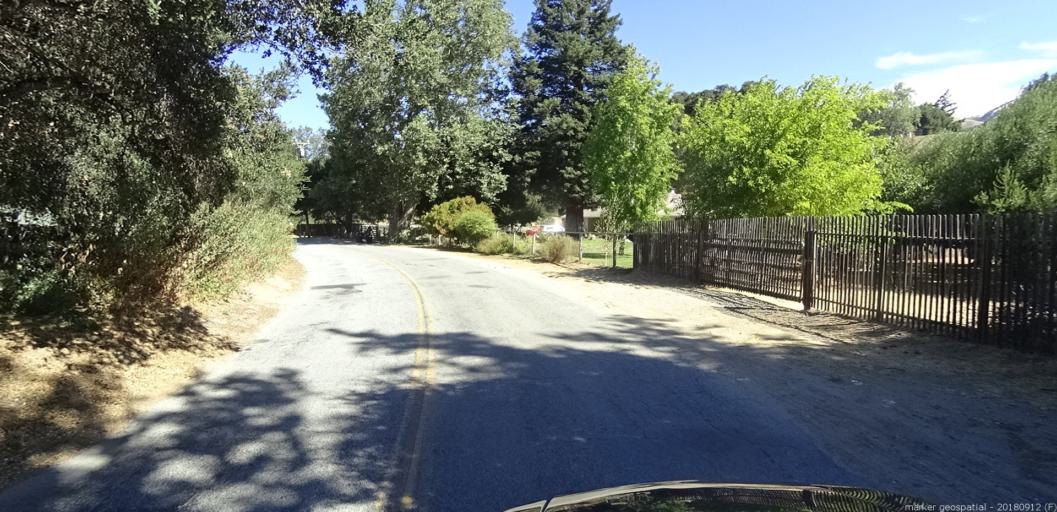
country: US
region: California
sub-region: Monterey County
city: Carmel Valley Village
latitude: 36.4905
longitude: -121.7474
